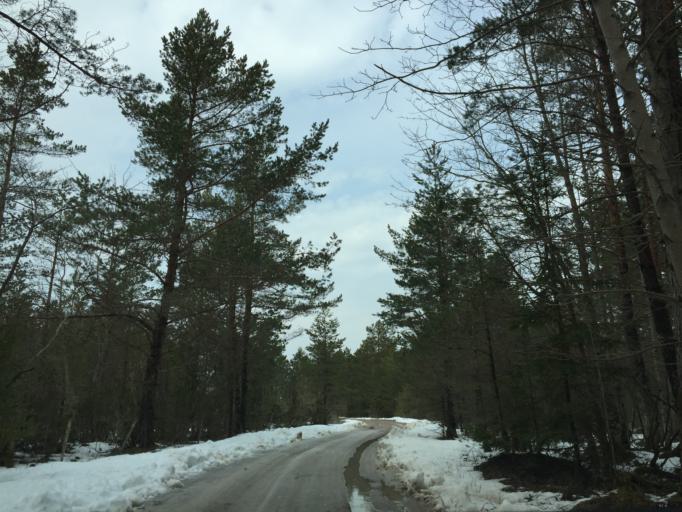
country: EE
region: Saare
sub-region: Kuressaare linn
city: Kuressaare
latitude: 58.4320
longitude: 22.1431
